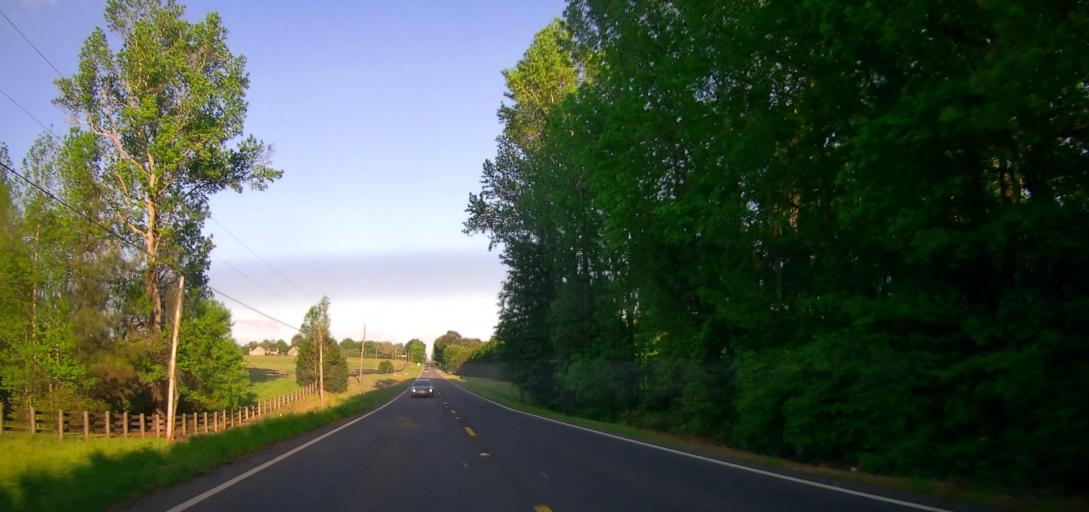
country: US
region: Georgia
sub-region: Walton County
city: Social Circle
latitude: 33.5069
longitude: -83.6637
